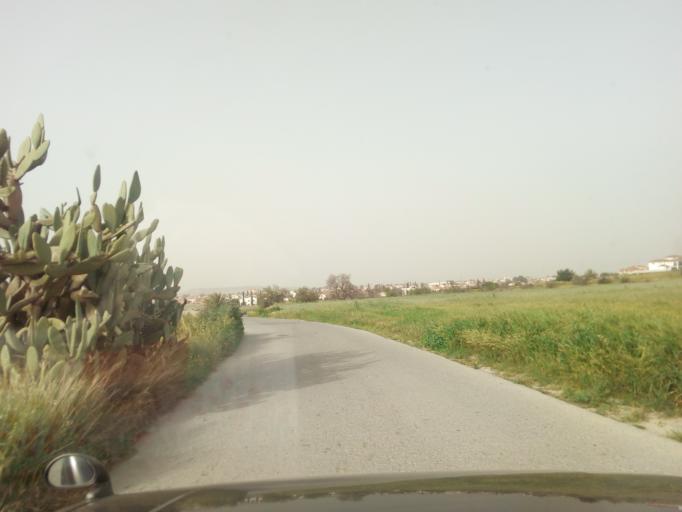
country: CY
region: Larnaka
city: Athienou
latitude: 35.0496
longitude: 33.5368
